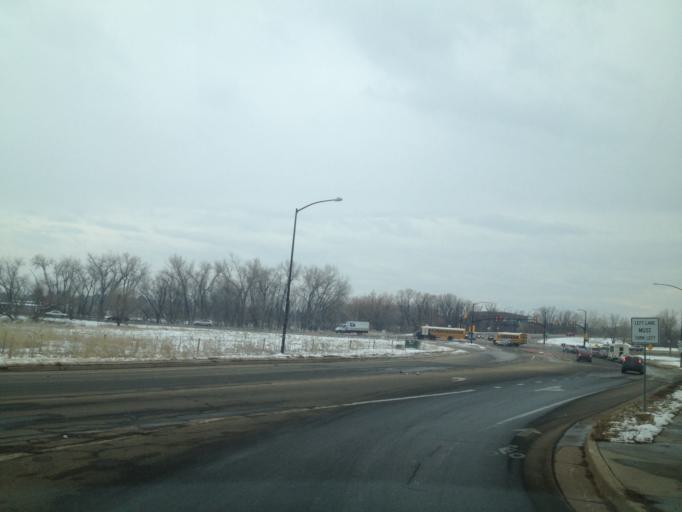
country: US
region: Colorado
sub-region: Boulder County
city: Boulder
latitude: 40.0291
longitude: -105.2256
